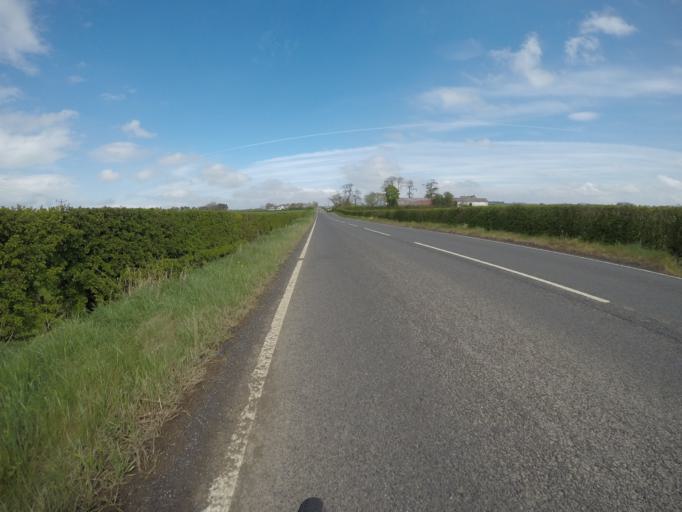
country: GB
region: Scotland
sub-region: East Ayrshire
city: Kilmaurs
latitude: 55.6590
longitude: -4.5525
